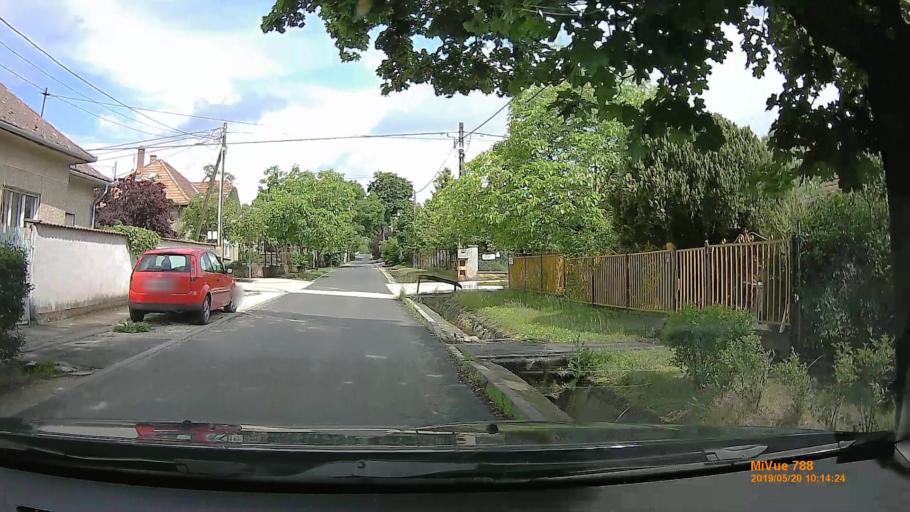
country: HU
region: Budapest
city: Budapest XVII. keruelet
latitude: 47.4904
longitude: 19.2763
